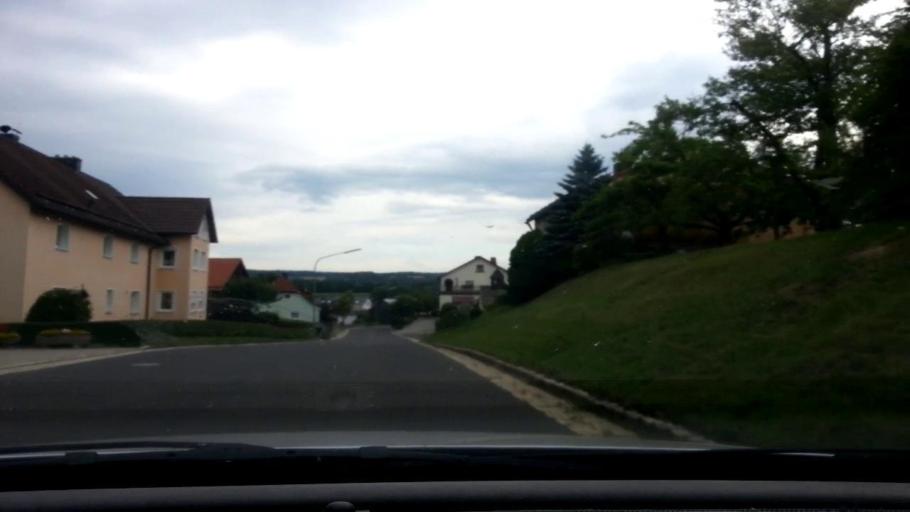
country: DE
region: Bavaria
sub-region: Upper Palatinate
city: Kulmain
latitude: 49.8918
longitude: 11.9290
